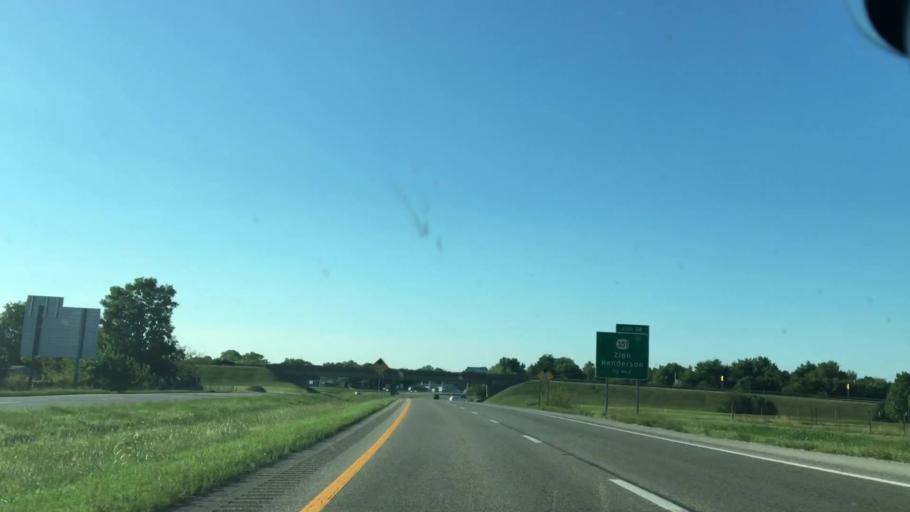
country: US
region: Kentucky
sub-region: Henderson County
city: Henderson
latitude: 37.8233
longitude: -87.5638
